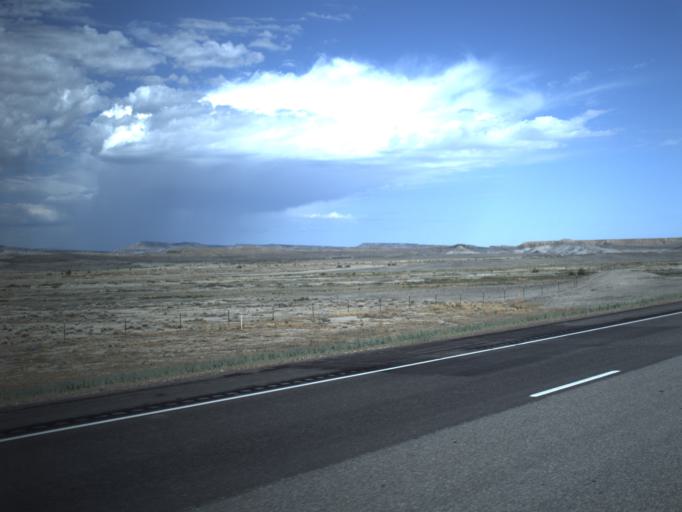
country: US
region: Utah
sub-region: Carbon County
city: East Carbon City
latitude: 39.3117
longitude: -110.3613
